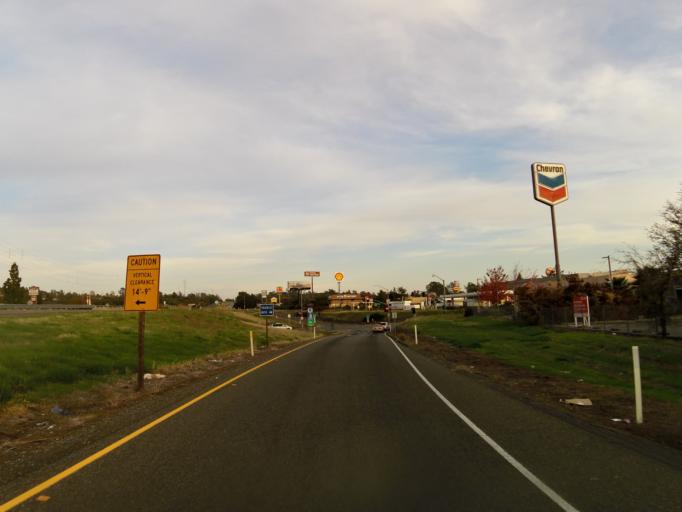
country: US
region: California
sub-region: El Dorado County
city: Cameron Park
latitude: 38.6592
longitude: -120.9704
